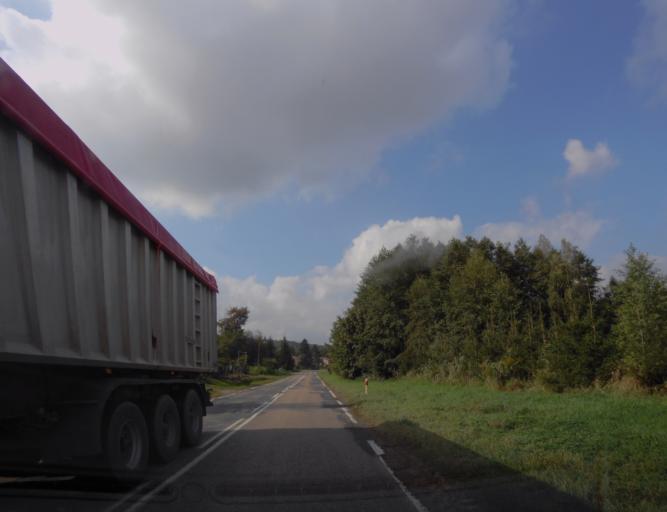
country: PL
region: Lublin Voivodeship
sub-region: Powiat krasnostawski
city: Krasnystaw
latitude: 50.9684
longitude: 23.1160
